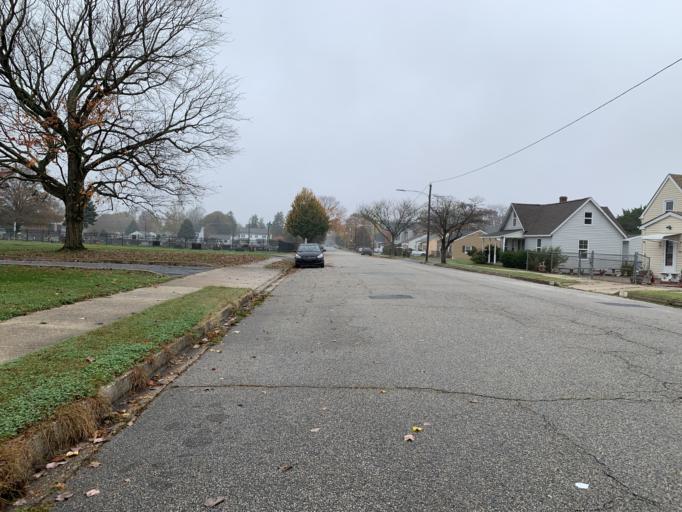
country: US
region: Delaware
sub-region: Kent County
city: Dover
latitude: 39.1661
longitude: -75.5315
